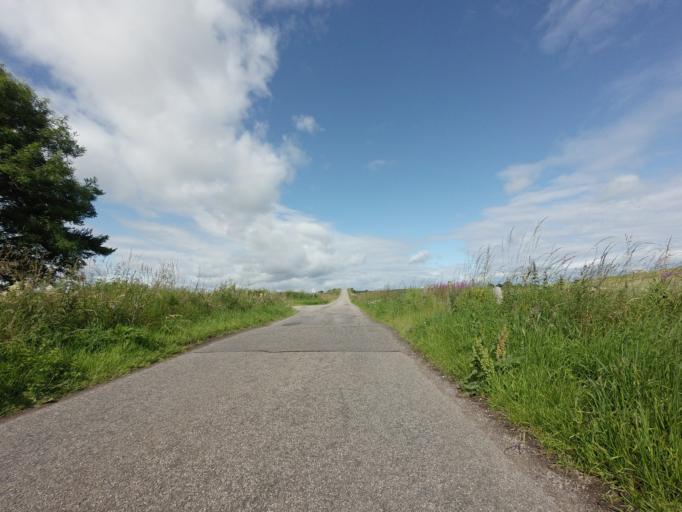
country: GB
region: Scotland
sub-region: Moray
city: Burghead
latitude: 57.6536
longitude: -3.4700
